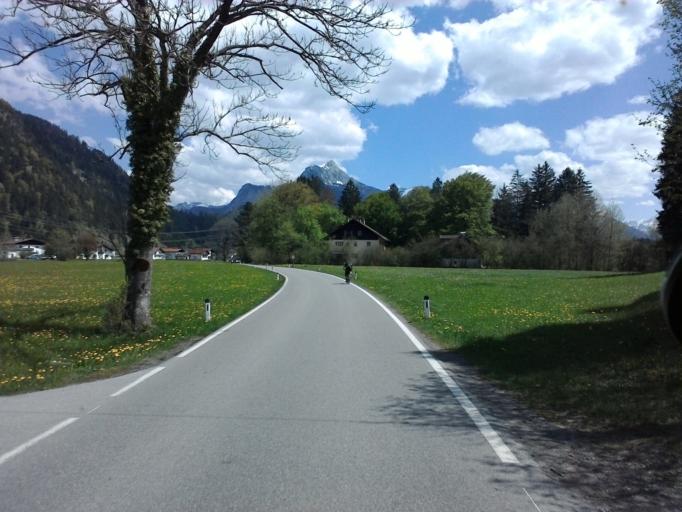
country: AT
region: Tyrol
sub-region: Politischer Bezirk Reutte
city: Musau
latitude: 47.5448
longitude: 10.6665
